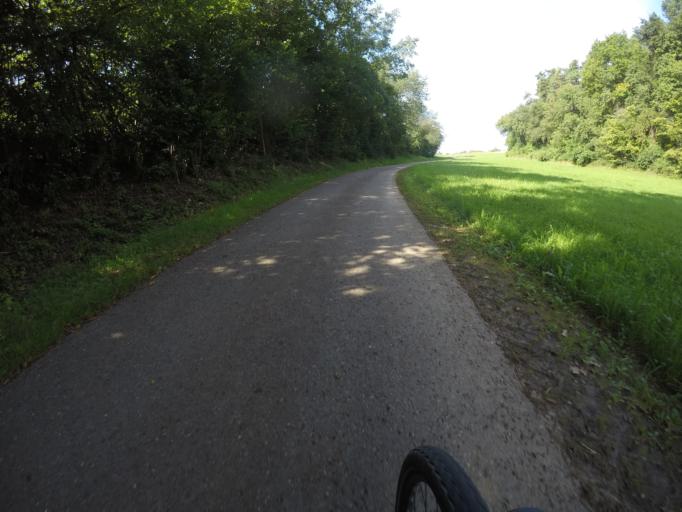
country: DE
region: Baden-Wuerttemberg
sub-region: Karlsruhe Region
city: Monsheim
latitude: 48.8797
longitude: 8.8770
